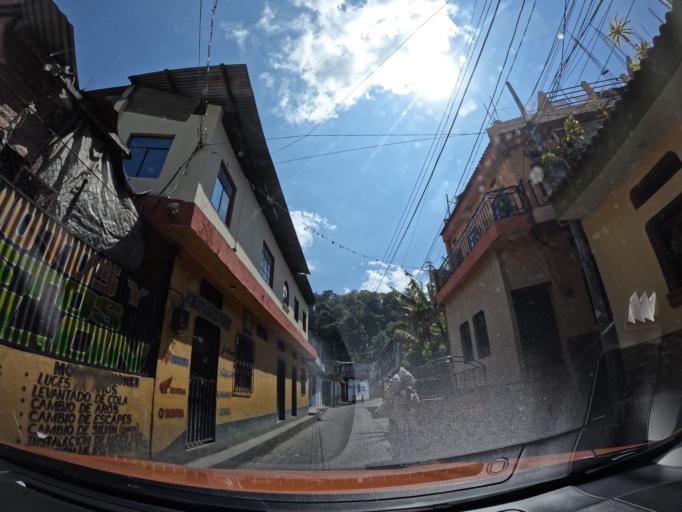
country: GT
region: Solola
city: Santiago Atitlan
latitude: 14.6347
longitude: -91.2302
